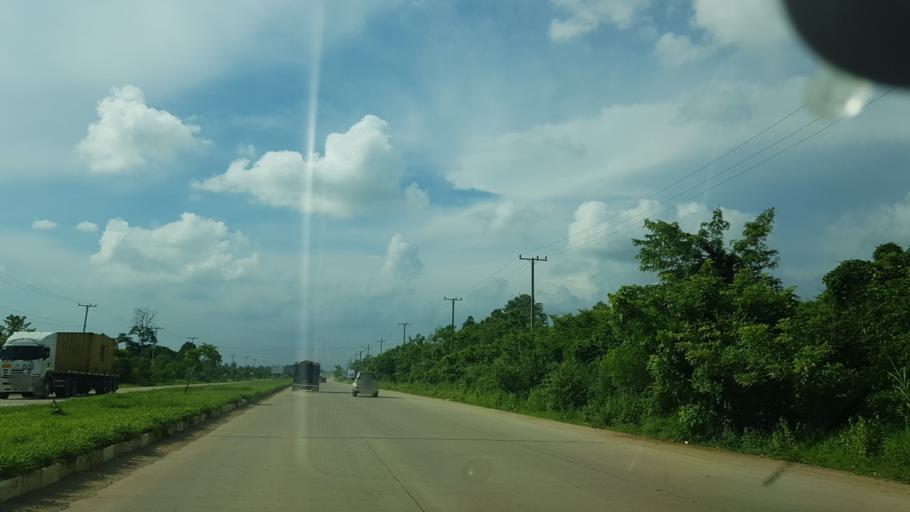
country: TH
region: Nong Khai
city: Nong Khai
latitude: 17.9226
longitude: 102.7195
